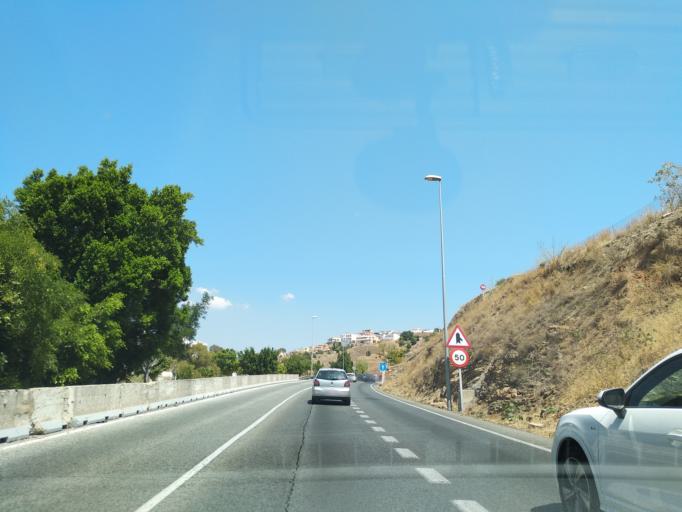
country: ES
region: Andalusia
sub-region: Provincia de Malaga
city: Malaga
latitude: 36.7383
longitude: -4.4182
